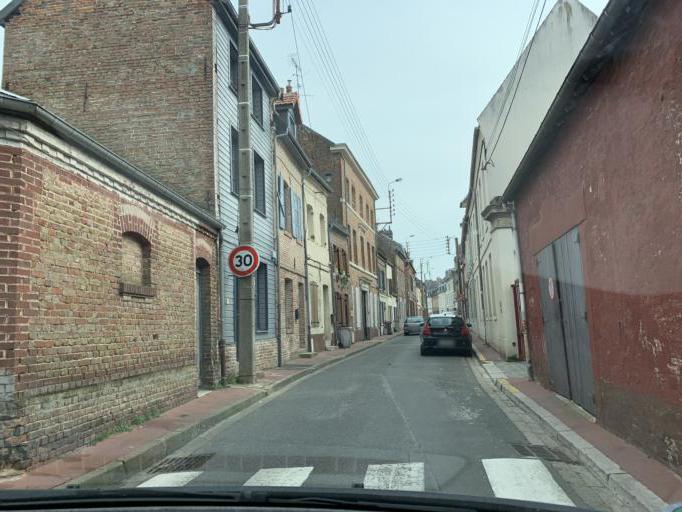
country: FR
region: Picardie
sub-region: Departement de la Somme
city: Abbeville
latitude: 50.1082
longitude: 1.8302
